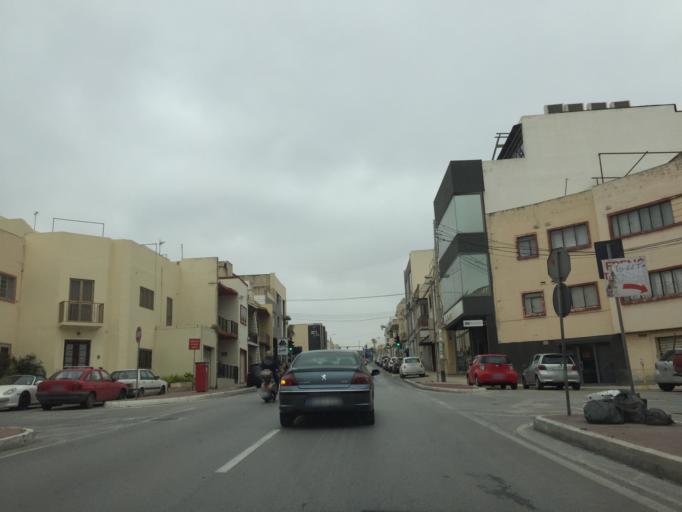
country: MT
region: Attard
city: Attard
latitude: 35.8895
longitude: 14.4416
